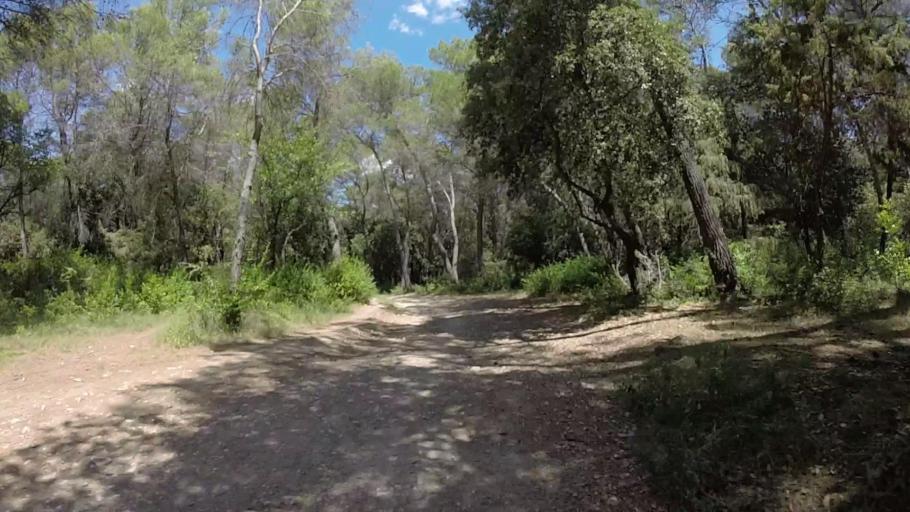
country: FR
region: Provence-Alpes-Cote d'Azur
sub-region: Departement des Alpes-Maritimes
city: Mougins
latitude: 43.5979
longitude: 7.0229
